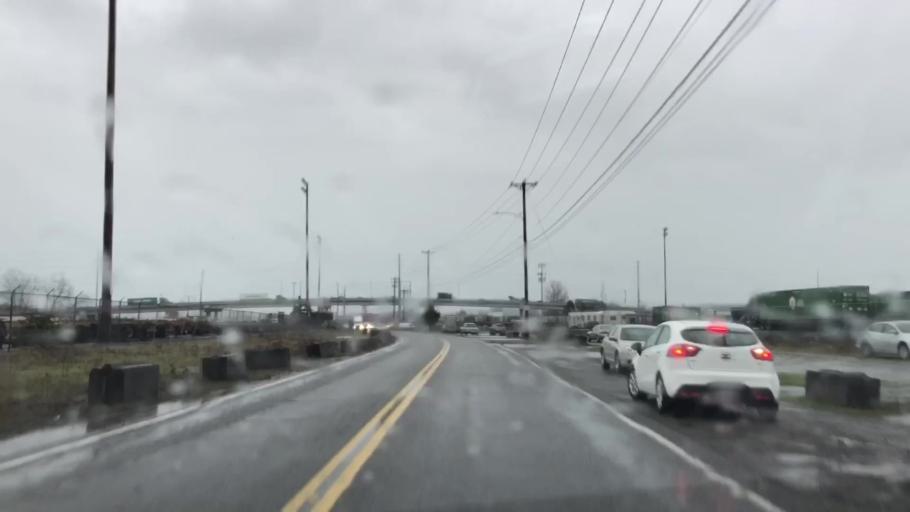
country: US
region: Washington
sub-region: Pierce County
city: Tacoma
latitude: 47.2589
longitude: -122.4082
